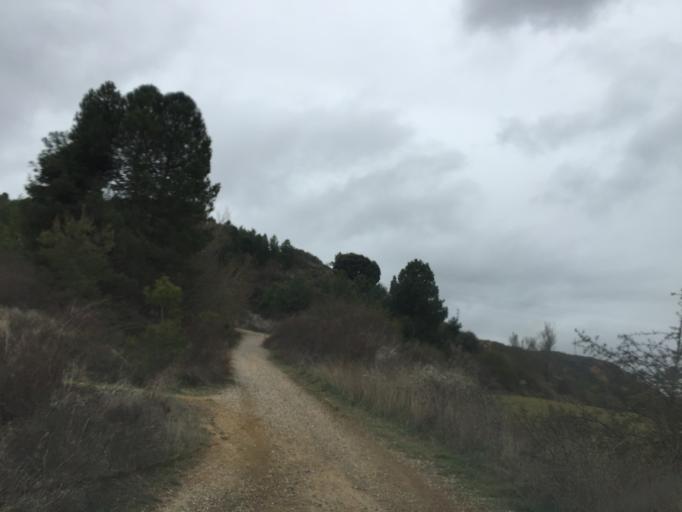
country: ES
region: Castille and Leon
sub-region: Provincia de Leon
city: Leon
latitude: 42.5995
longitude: -5.5407
